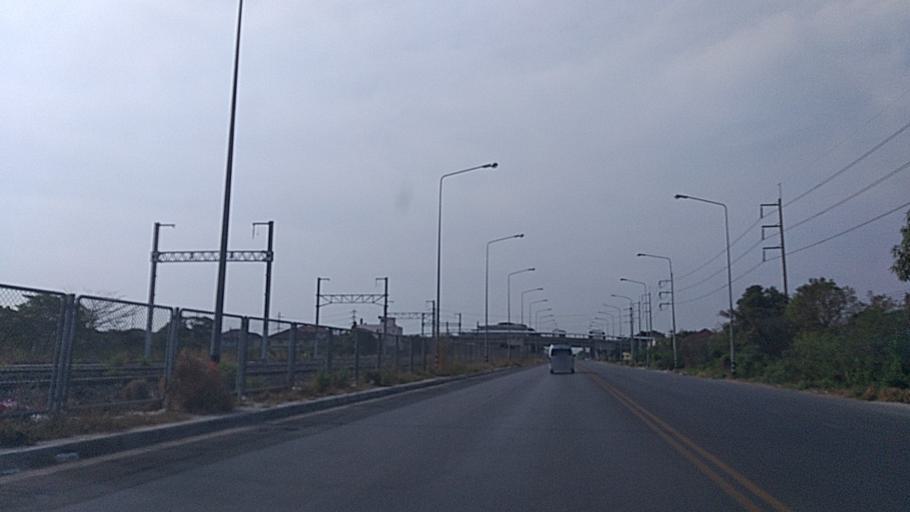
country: TH
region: Bangkok
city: Don Mueang
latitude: 13.9699
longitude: 100.6046
